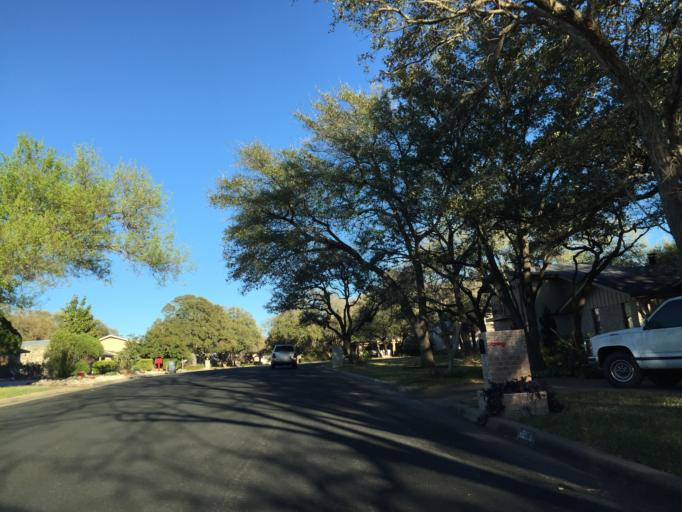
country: US
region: Texas
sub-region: Williamson County
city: Jollyville
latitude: 30.4380
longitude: -97.7877
